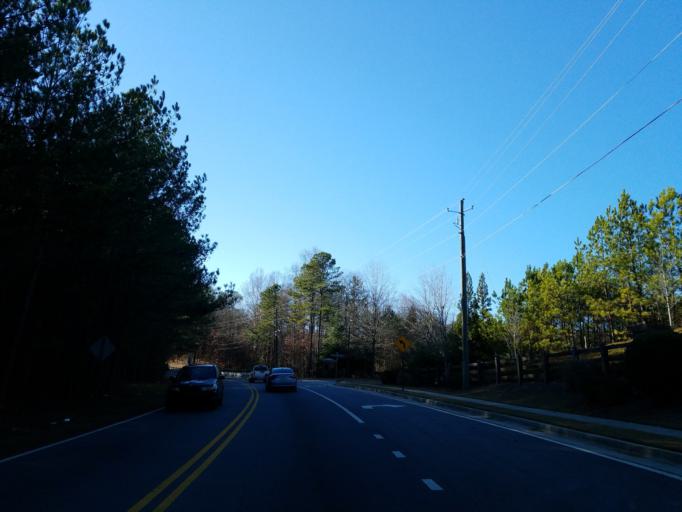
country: US
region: Georgia
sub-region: Cobb County
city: Mableton
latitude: 33.7773
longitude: -84.5583
